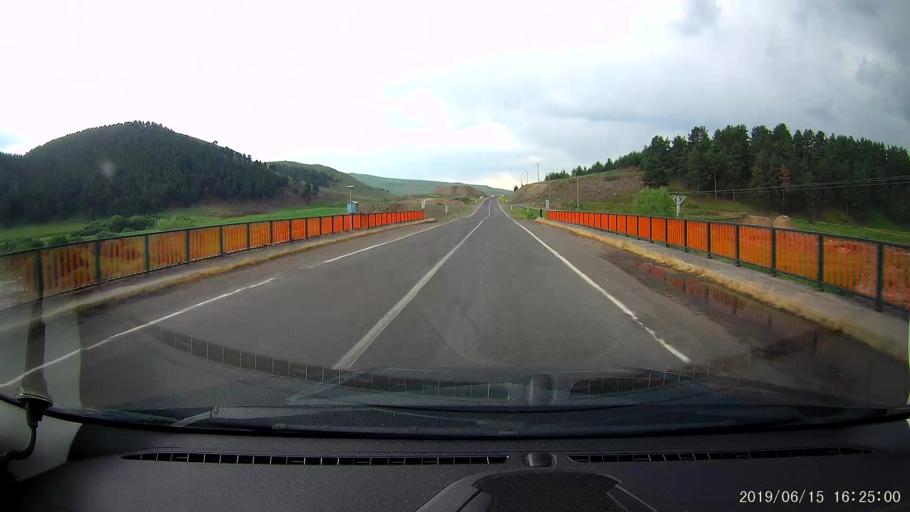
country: TR
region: Ardahan
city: Hanak
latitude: 41.1595
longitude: 42.8718
